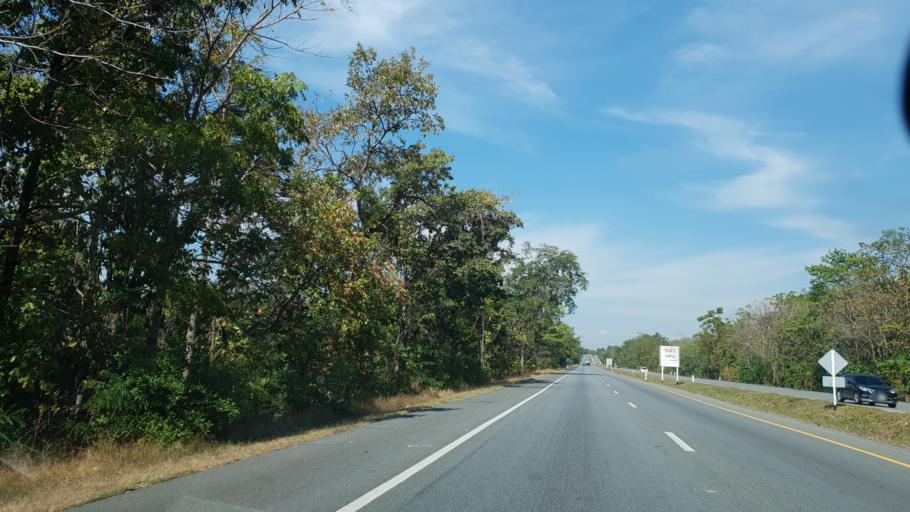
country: TH
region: Uttaradit
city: Thong Saen Khan
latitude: 17.4094
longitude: 100.2293
